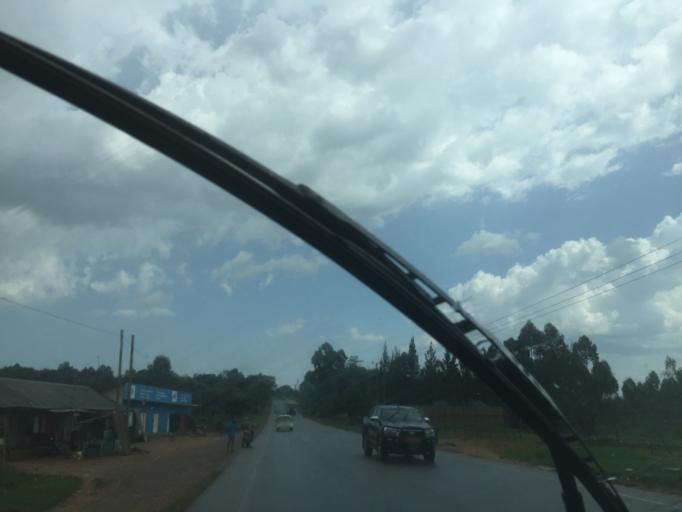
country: UG
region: Central Region
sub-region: Wakiso District
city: Wakiso
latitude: 0.5582
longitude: 32.5307
